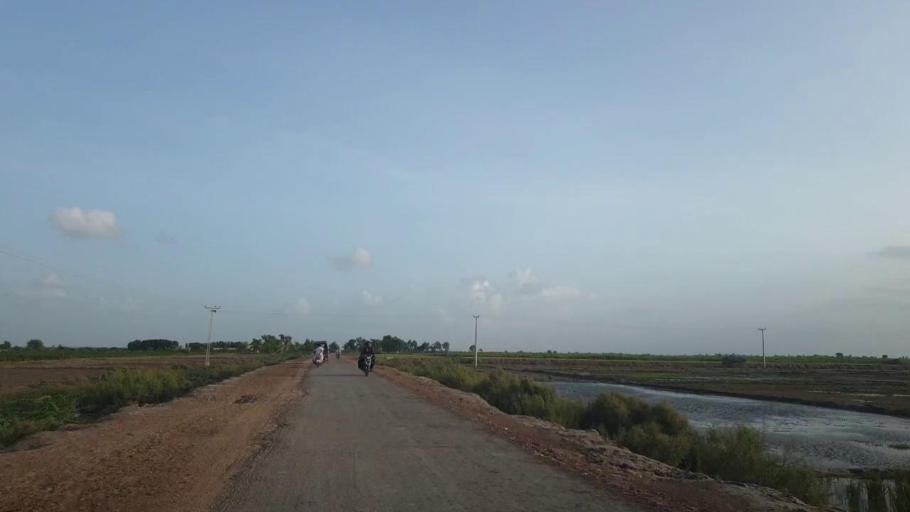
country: PK
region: Sindh
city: Kadhan
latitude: 24.6207
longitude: 69.1158
